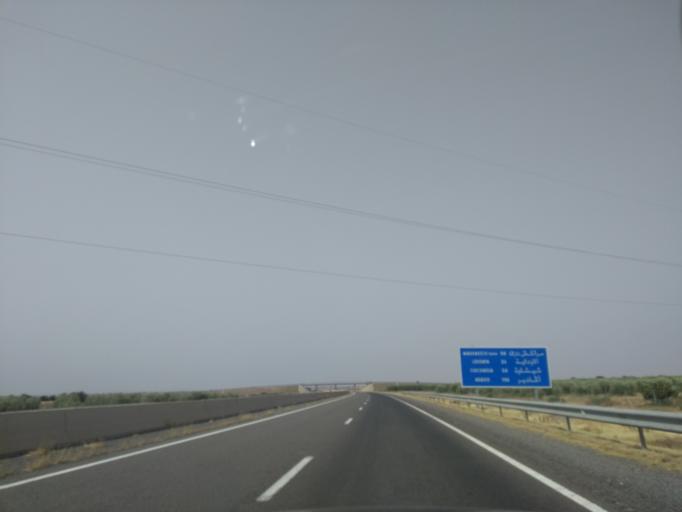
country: MA
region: Marrakech-Tensift-Al Haouz
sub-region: Marrakech
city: Marrakesh
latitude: 31.7447
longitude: -8.2095
